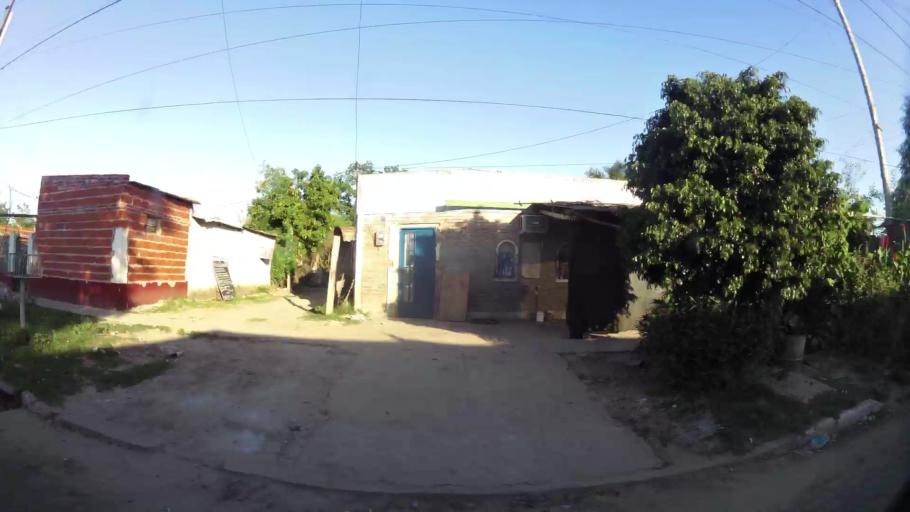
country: AR
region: Santa Fe
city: Santa Fe de la Vera Cruz
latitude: -31.5971
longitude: -60.6770
